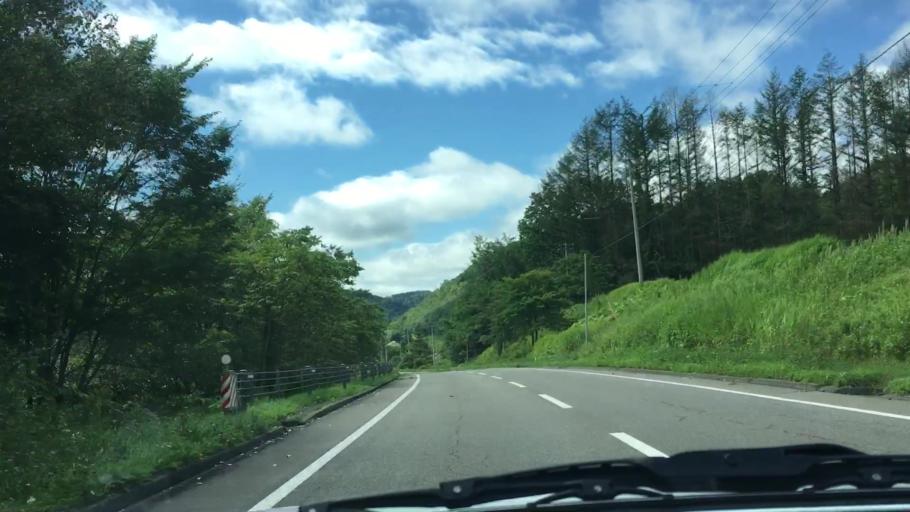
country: JP
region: Hokkaido
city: Kitami
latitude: 43.3685
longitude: 143.8627
